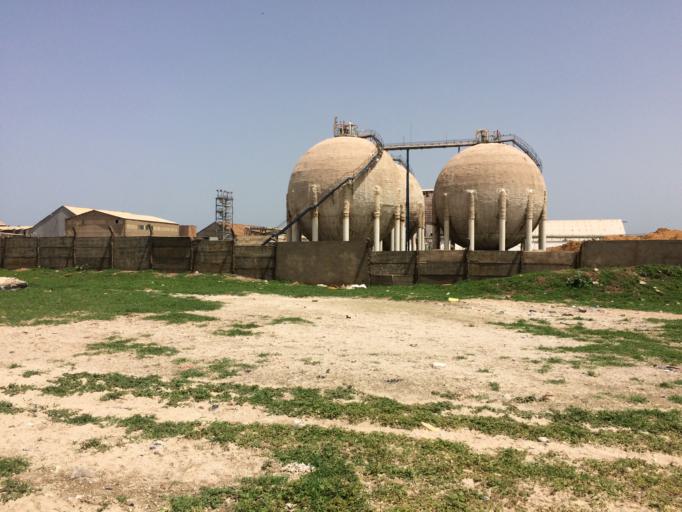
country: SN
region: Dakar
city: Pikine
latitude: 14.7353
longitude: -17.3417
